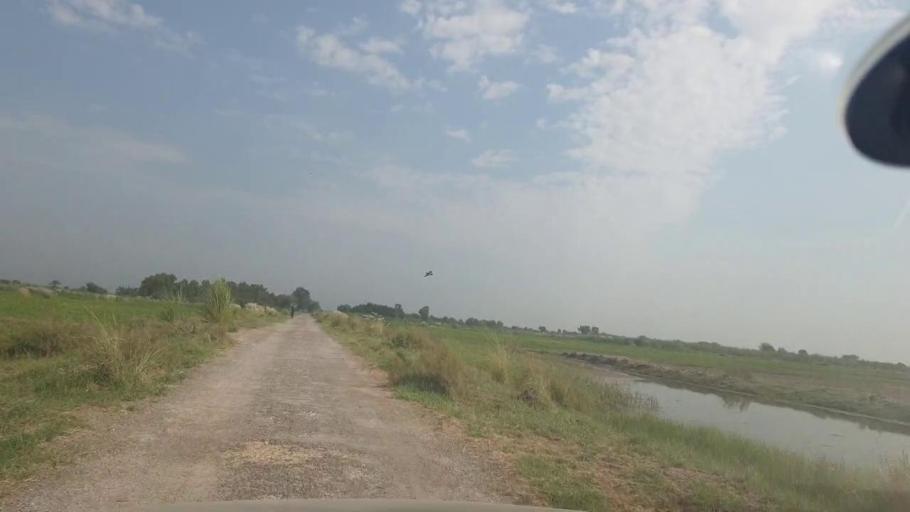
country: PK
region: Balochistan
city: Mehrabpur
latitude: 28.0489
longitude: 68.1227
